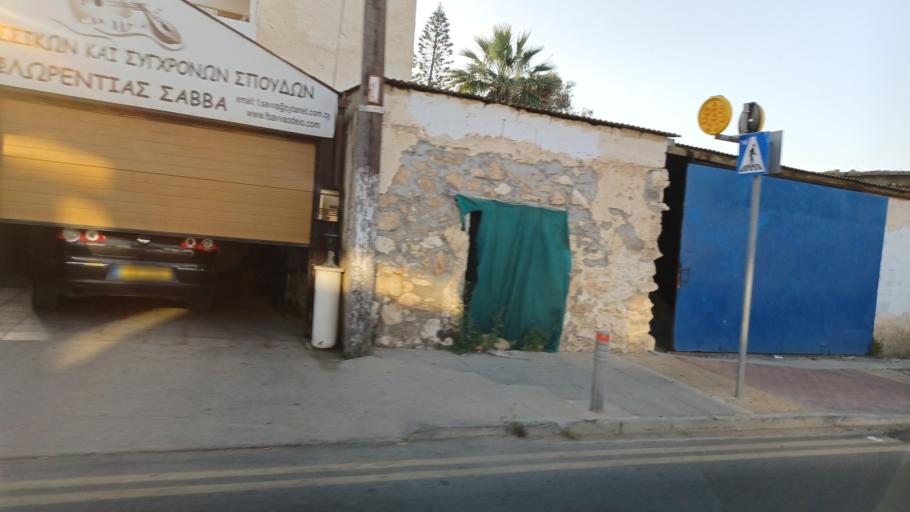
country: CY
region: Ammochostos
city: Frenaros
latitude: 35.0271
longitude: 33.9514
